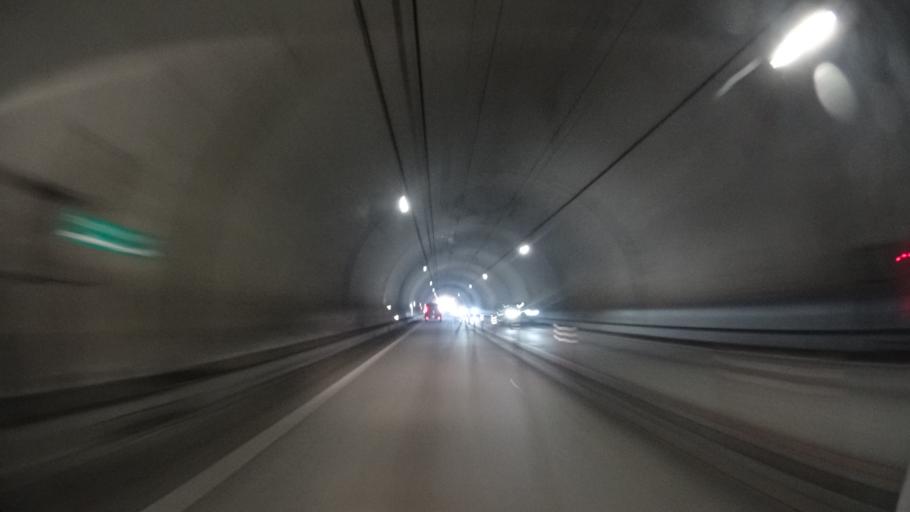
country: JP
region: Yamaguchi
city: Nagato
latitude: 34.3670
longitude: 131.2644
